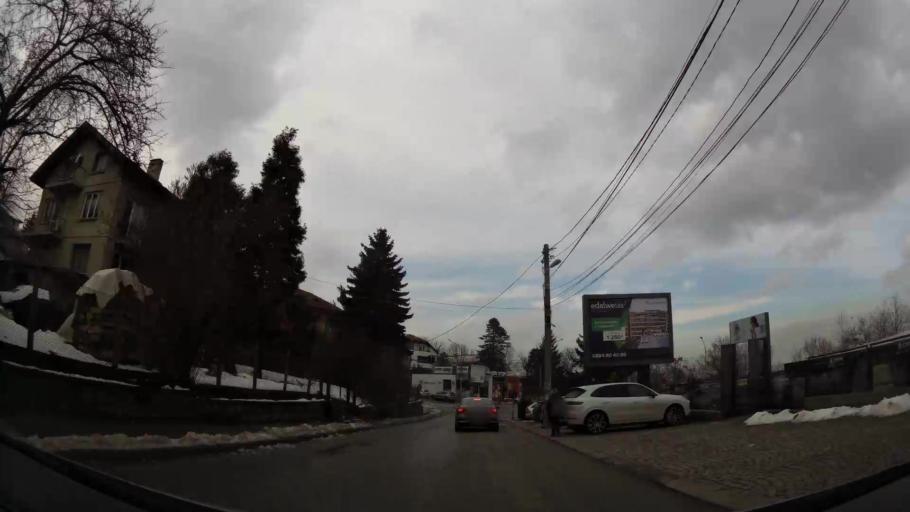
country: BG
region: Sofia-Capital
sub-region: Stolichna Obshtina
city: Sofia
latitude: 42.6493
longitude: 23.2614
